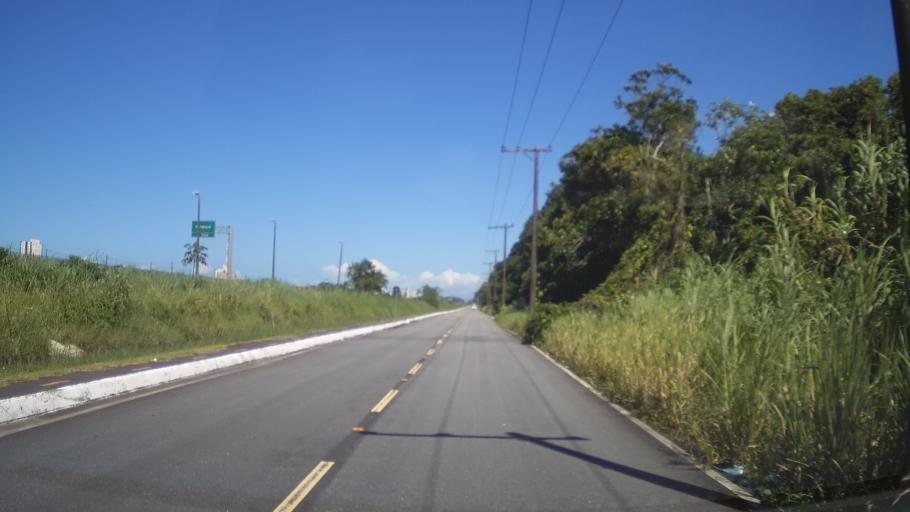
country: BR
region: Sao Paulo
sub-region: Mongagua
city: Mongagua
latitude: -24.0703
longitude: -46.5791
